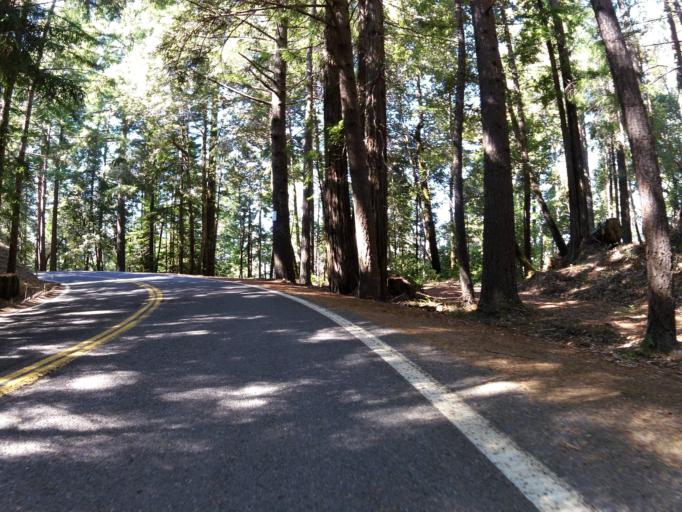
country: US
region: California
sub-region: Humboldt County
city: Redway
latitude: 39.8320
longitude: -123.7761
